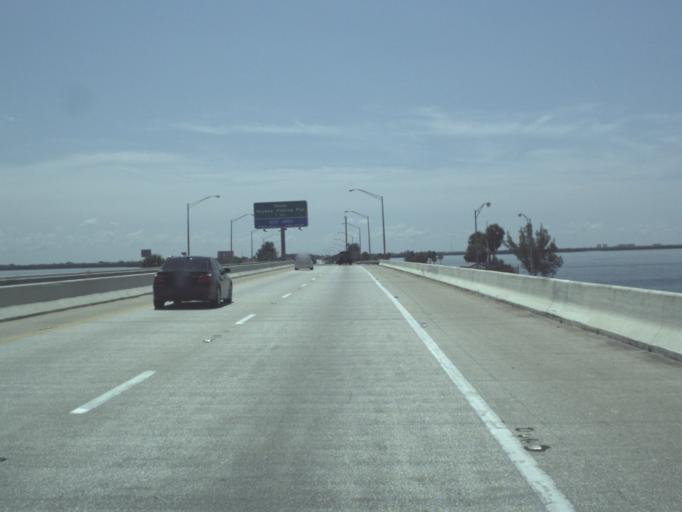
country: US
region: Florida
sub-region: Manatee County
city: Memphis
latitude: 27.5932
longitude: -82.6312
